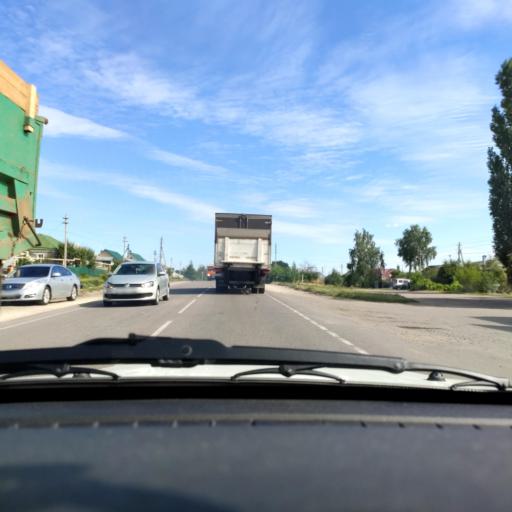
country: RU
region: Voronezj
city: Orlovo
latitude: 51.7541
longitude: 39.5879
